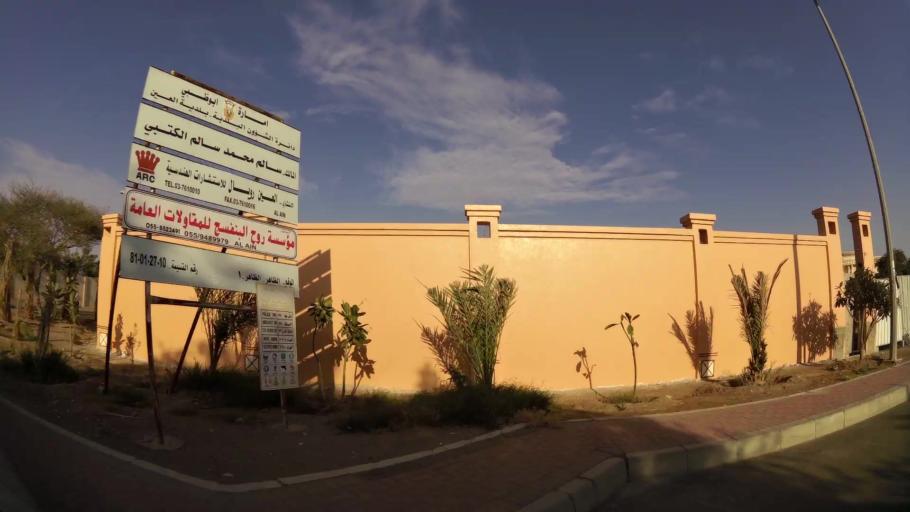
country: AE
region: Abu Dhabi
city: Al Ain
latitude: 24.0856
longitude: 55.8442
